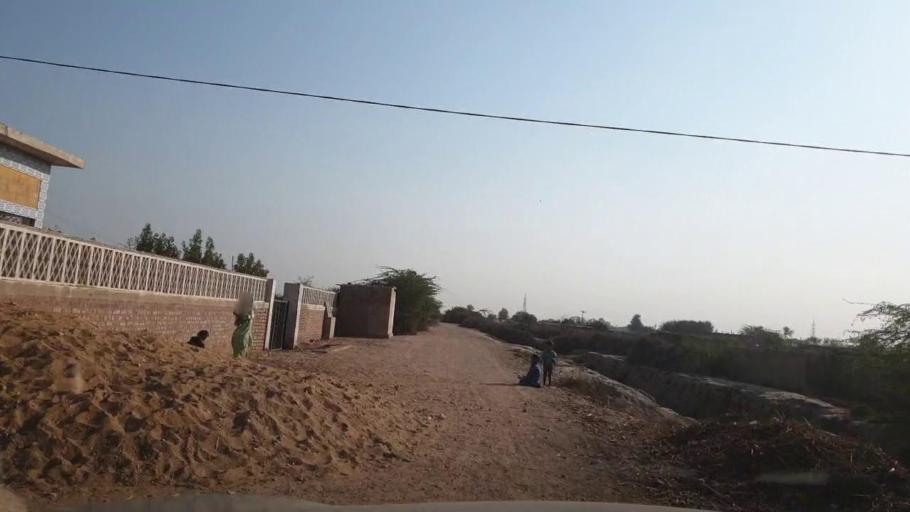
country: PK
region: Sindh
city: Tando Allahyar
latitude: 25.5059
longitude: 68.8400
